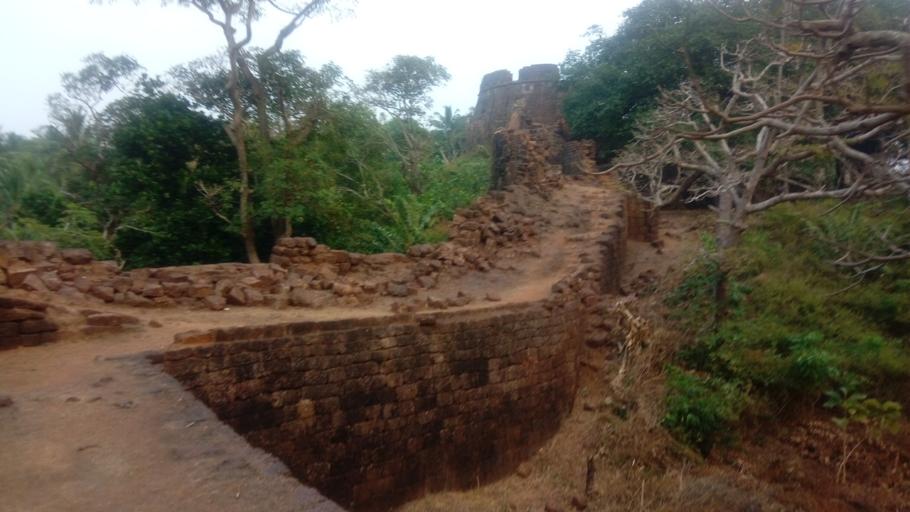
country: IN
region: Goa
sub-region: South Goa
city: Cavelossim
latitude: 15.0897
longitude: 73.9208
